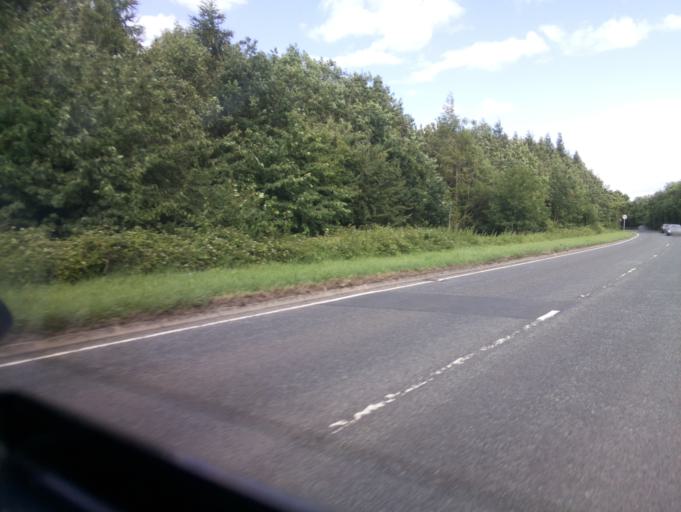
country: GB
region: England
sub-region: Leicestershire
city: Ashby de la Zouch
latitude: 52.7509
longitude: -1.4310
